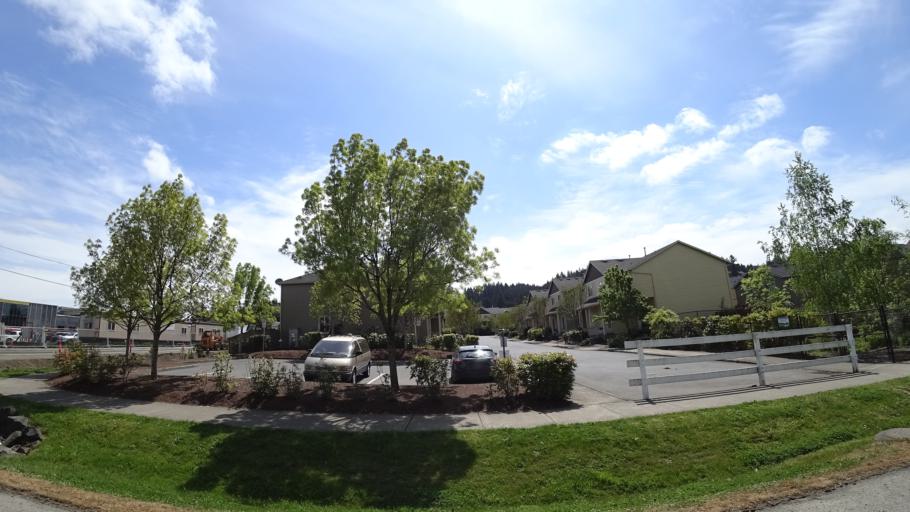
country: US
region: Oregon
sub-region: Washington County
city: Aloha
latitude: 45.4691
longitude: -122.8853
